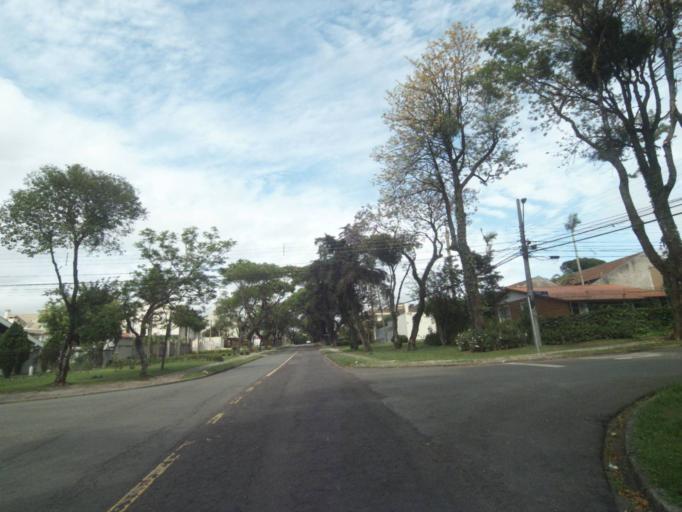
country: BR
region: Parana
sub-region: Curitiba
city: Curitiba
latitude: -25.4241
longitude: -49.2314
